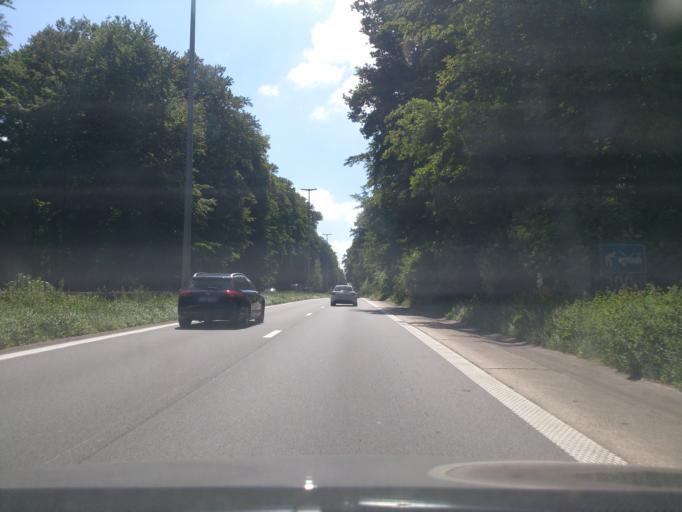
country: BE
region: Flanders
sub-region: Provincie Vlaams-Brabant
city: Hoeilaart
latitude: 50.7557
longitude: 4.4356
